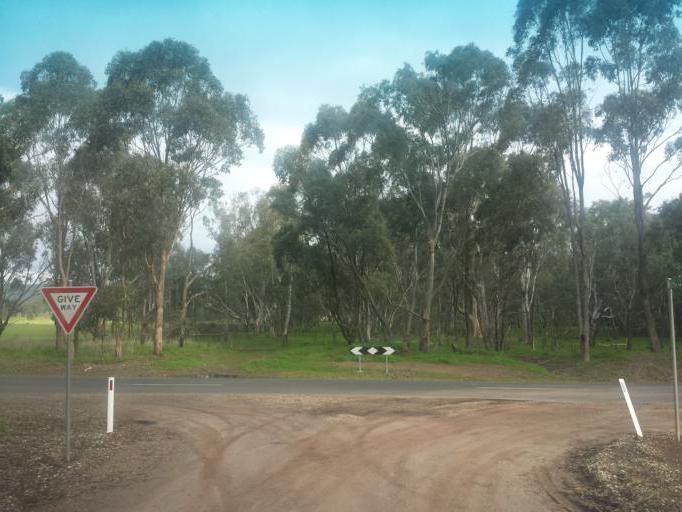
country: AU
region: Victoria
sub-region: Murrindindi
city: Kinglake West
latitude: -37.0465
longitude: 145.2319
